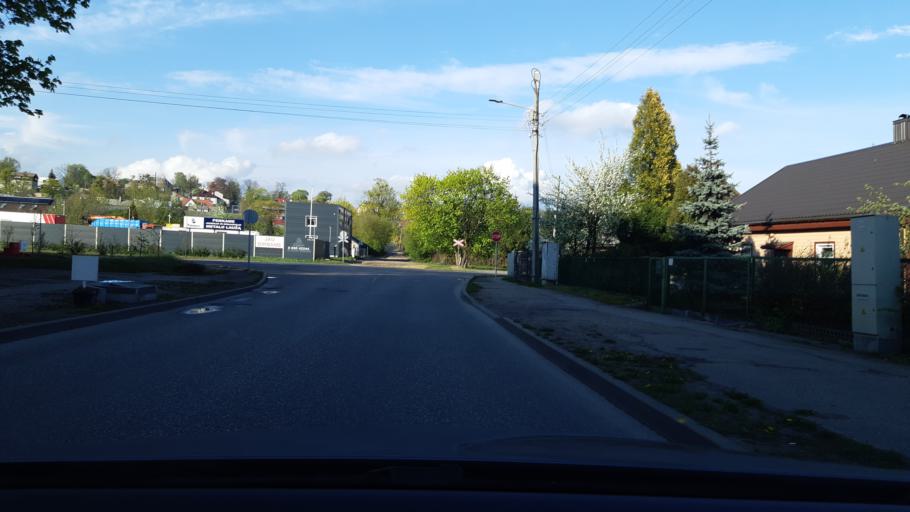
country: LT
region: Kauno apskritis
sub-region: Kaunas
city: Aleksotas
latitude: 54.8708
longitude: 23.9436
